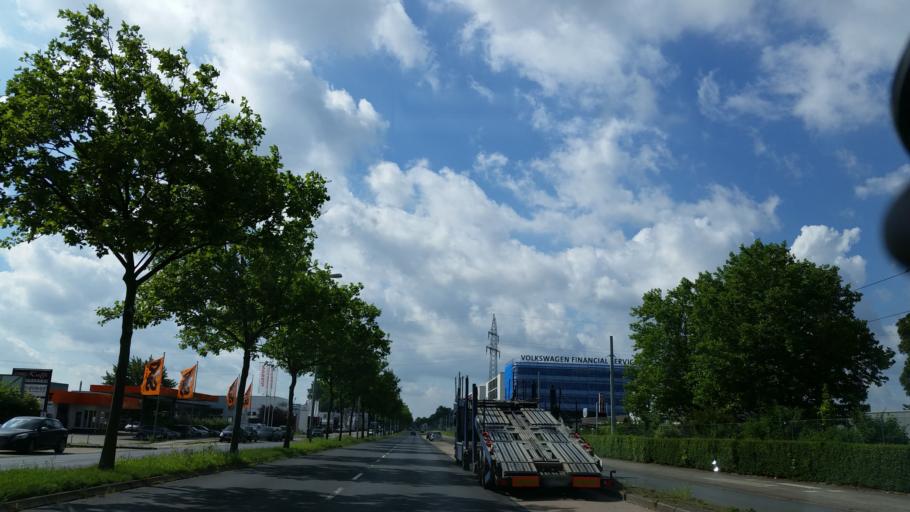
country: DE
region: Lower Saxony
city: Braunschweig
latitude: 52.3028
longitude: 10.5162
